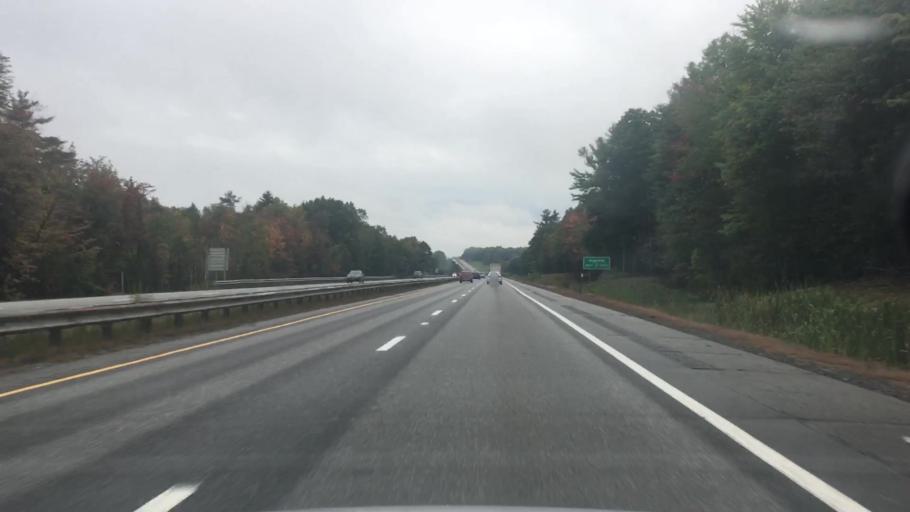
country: US
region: Maine
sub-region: Kennebec County
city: Hallowell
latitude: 44.2674
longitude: -69.8065
